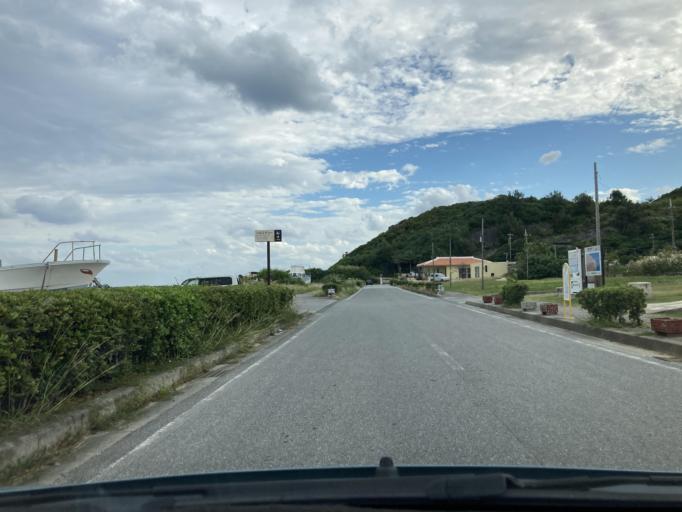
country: JP
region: Okinawa
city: Katsuren-haebaru
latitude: 26.3232
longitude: 127.9662
